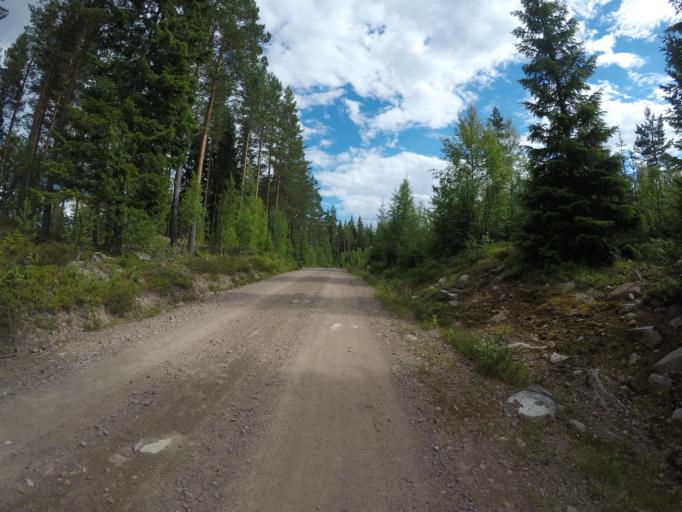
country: SE
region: Vaermland
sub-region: Filipstads Kommun
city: Lesjofors
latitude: 60.0809
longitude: 14.4245
